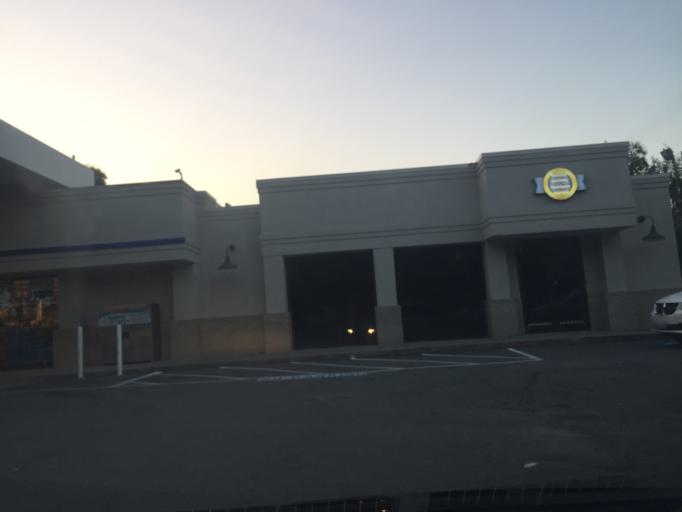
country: US
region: Georgia
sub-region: Chatham County
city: Thunderbolt
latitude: 32.0689
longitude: -81.0574
